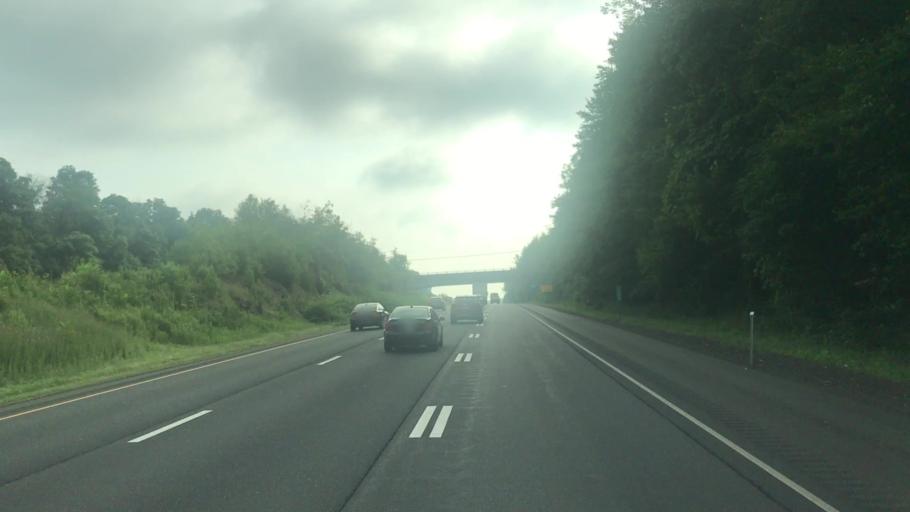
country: US
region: Connecticut
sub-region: New Haven County
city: Southbury
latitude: 41.4882
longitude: -73.1763
